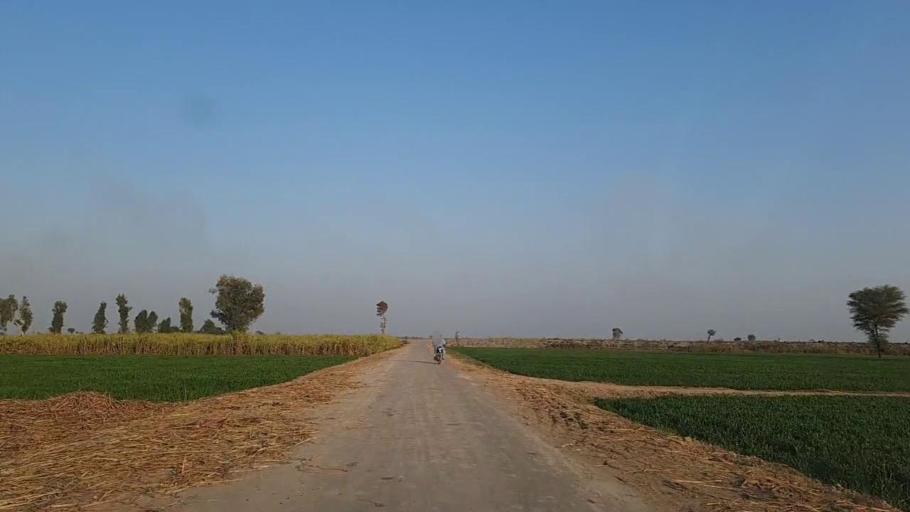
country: PK
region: Sindh
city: Daur
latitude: 26.5063
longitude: 68.2852
